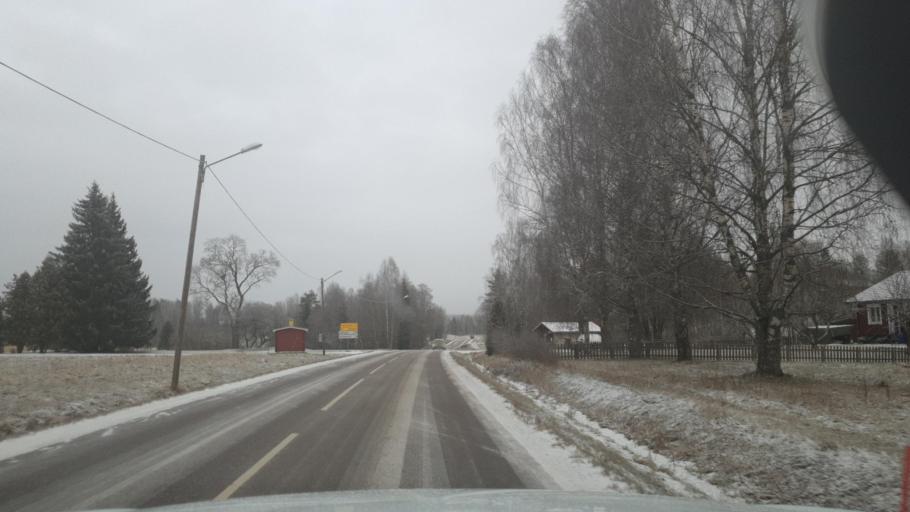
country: SE
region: Vaermland
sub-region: Arvika Kommun
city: Arvika
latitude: 59.6402
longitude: 12.8873
